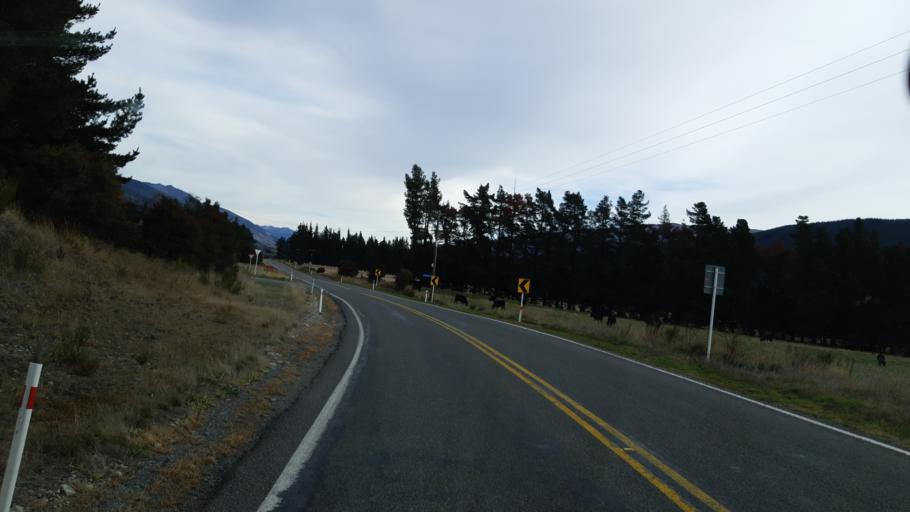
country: NZ
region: Tasman
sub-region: Tasman District
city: Brightwater
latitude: -41.6674
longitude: 173.1954
